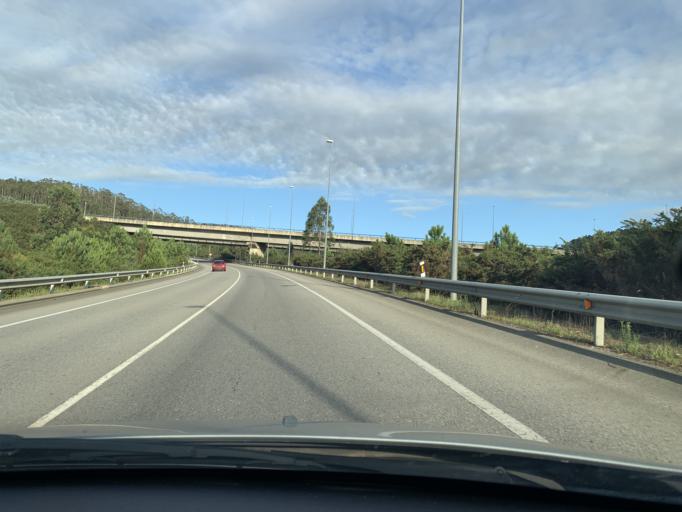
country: ES
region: Galicia
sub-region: Provincia de Lugo
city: Barreiros
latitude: 43.5318
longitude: -7.2512
